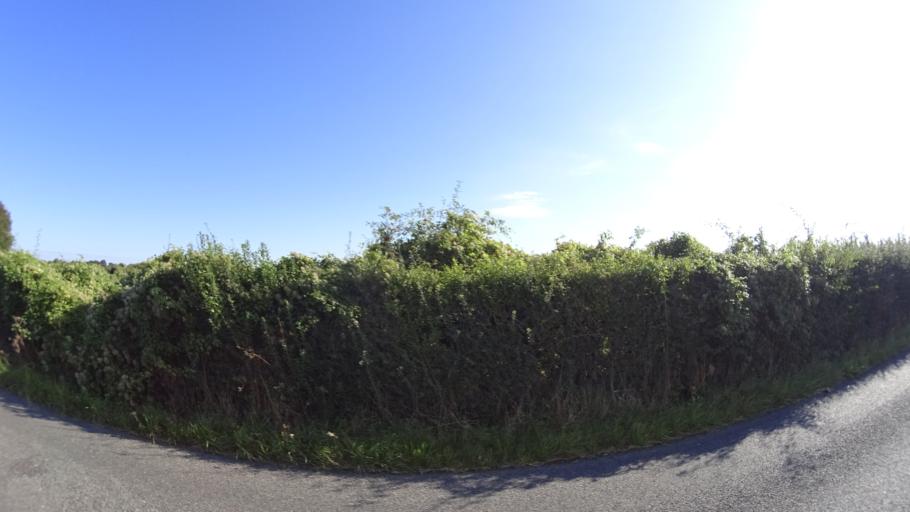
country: GB
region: England
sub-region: Hampshire
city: Abbotts Ann
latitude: 51.1463
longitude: -1.5388
